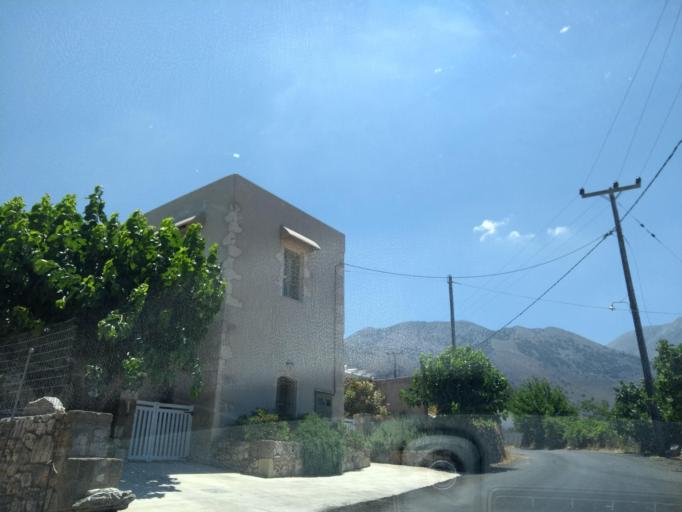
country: GR
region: Crete
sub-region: Nomos Chanias
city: Georgioupolis
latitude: 35.3136
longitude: 24.3100
